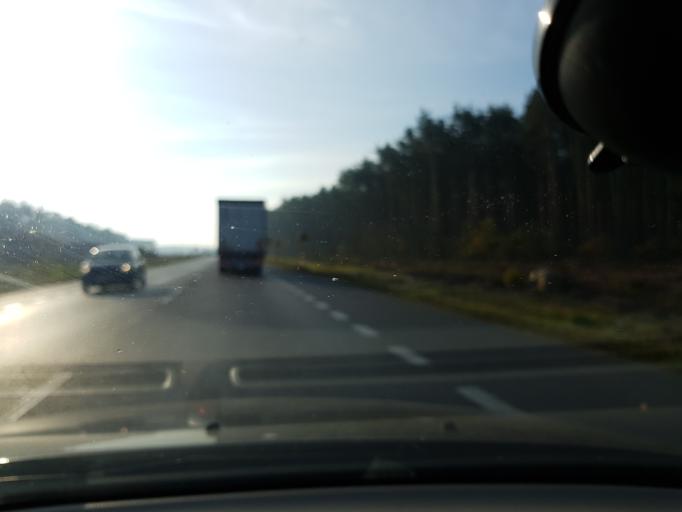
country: PL
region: Masovian Voivodeship
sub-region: Powiat otwocki
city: Otwock
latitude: 52.1572
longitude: 21.3085
